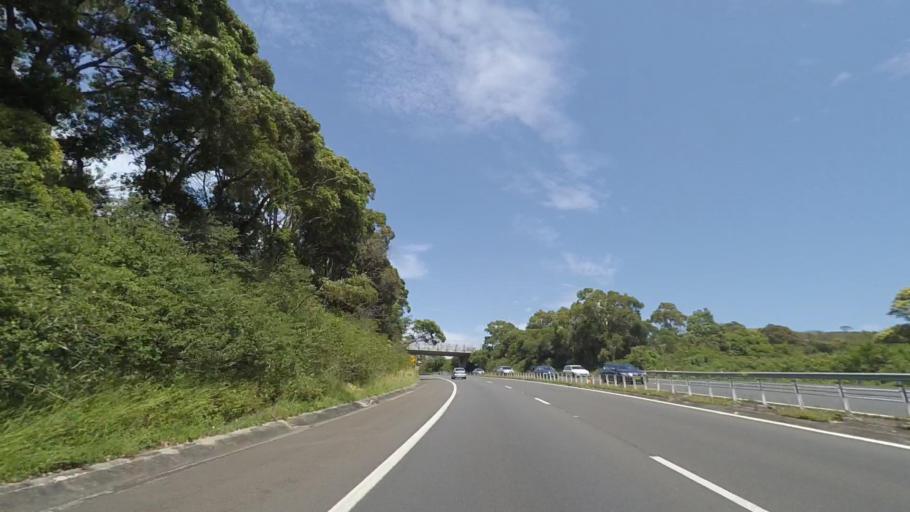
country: AU
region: New South Wales
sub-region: Kiama
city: Kiama
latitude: -34.6950
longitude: 150.8434
